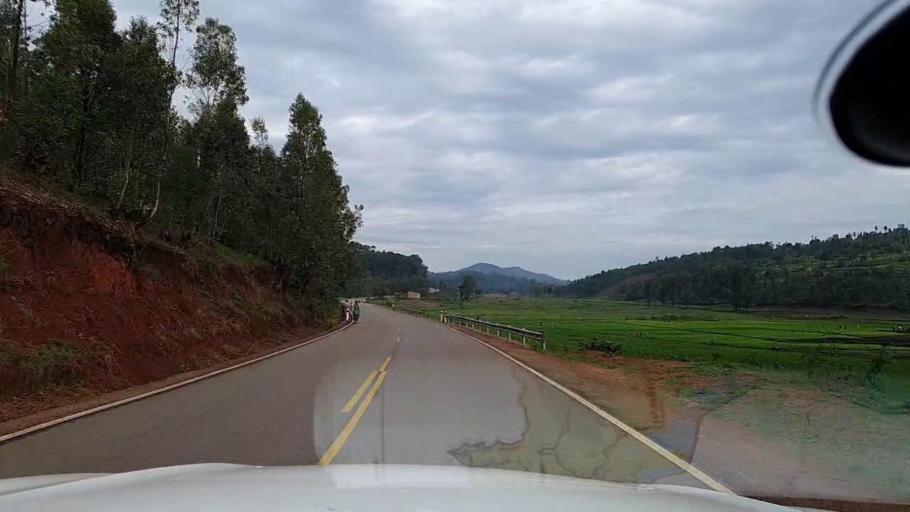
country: RW
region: Southern Province
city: Butare
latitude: -2.5673
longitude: 29.7277
